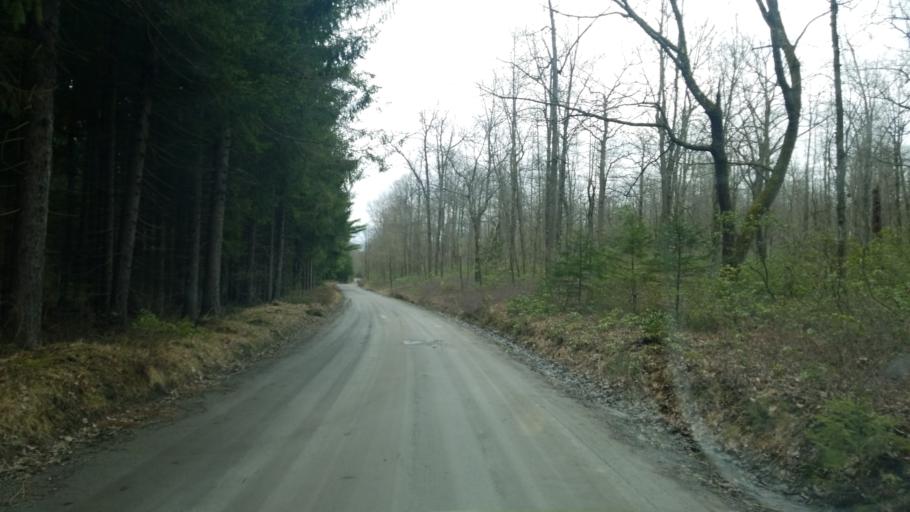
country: US
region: Pennsylvania
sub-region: Clearfield County
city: Shiloh
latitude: 41.1688
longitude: -78.2584
